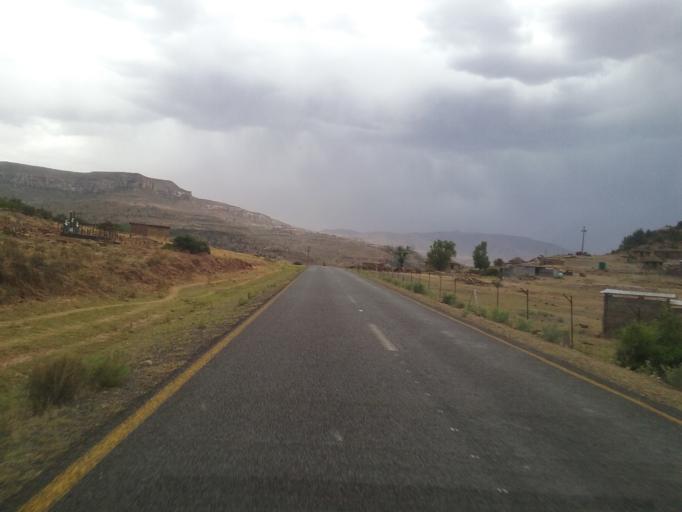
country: LS
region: Quthing
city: Quthing
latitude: -30.2865
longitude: 27.8085
